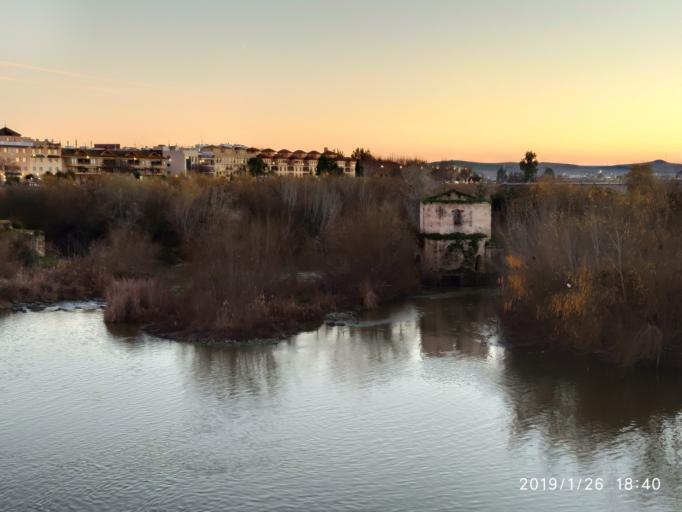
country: ES
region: Andalusia
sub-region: Province of Cordoba
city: Cordoba
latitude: 37.8770
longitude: -4.7784
